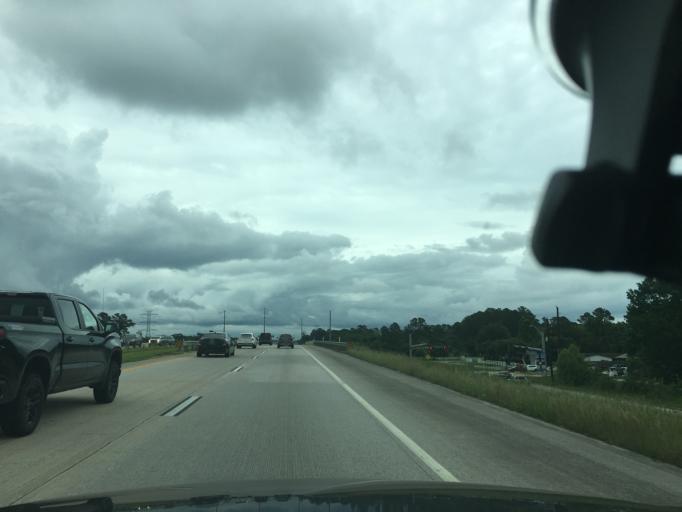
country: US
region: Texas
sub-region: Montgomery County
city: The Woodlands
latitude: 30.0944
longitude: -95.5082
